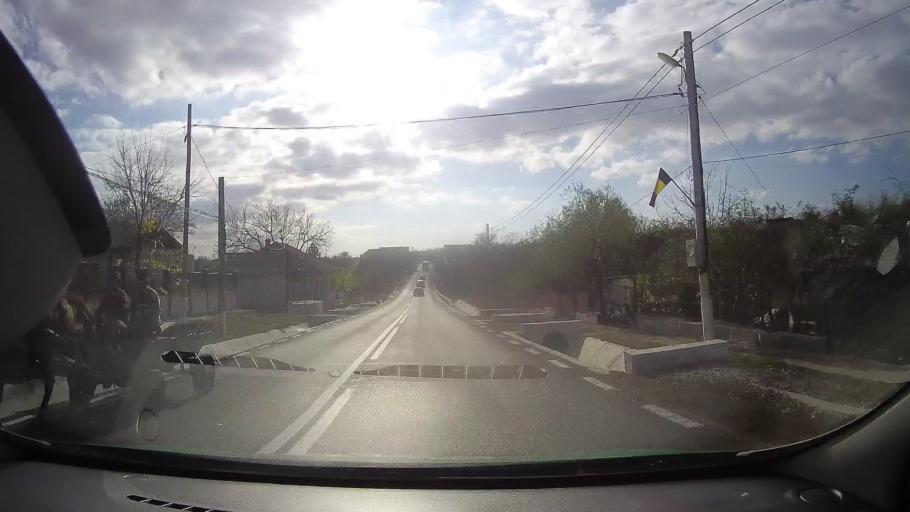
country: RO
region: Tulcea
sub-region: Comuna Topolog
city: Topolog
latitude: 44.8822
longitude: 28.3787
